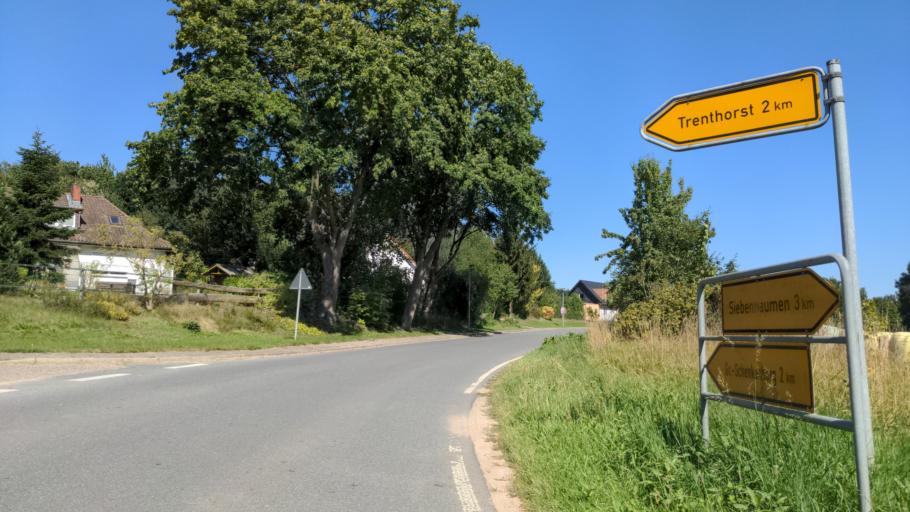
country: DE
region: Schleswig-Holstein
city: Grinau
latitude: 53.7766
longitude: 10.5478
